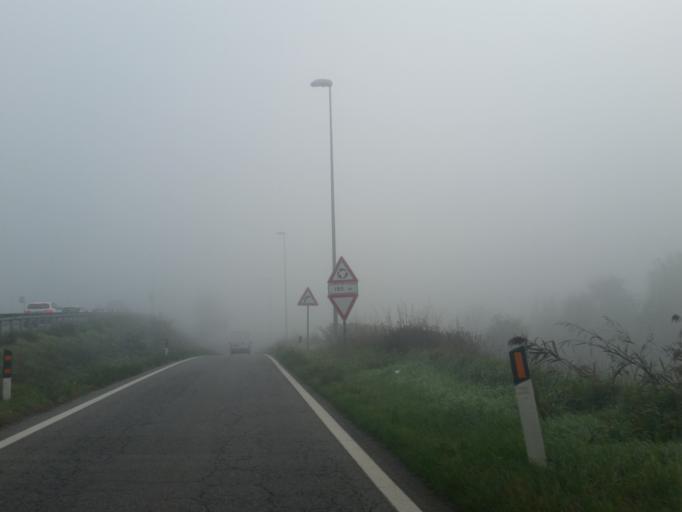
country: IT
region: Lombardy
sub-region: Provincia di Brescia
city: Barbariga
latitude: 45.3798
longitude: 10.0549
